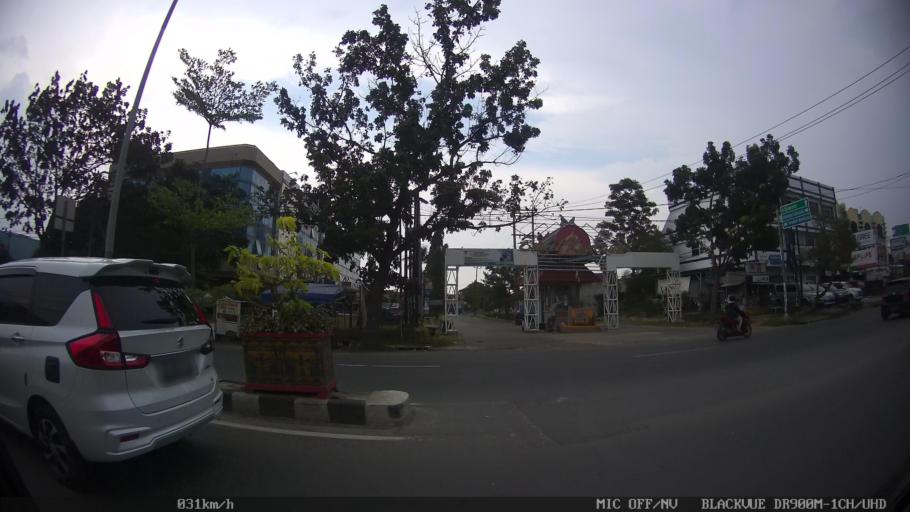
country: ID
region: Lampung
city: Kedaton
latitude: -5.3998
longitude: 105.2870
